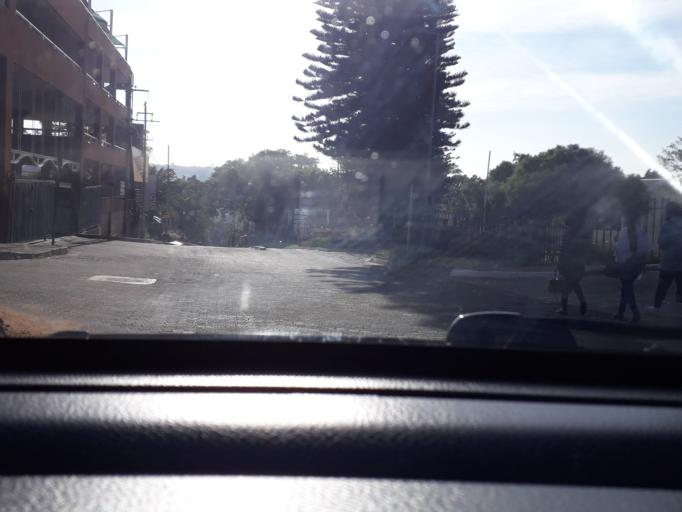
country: ZA
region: Gauteng
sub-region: City of Johannesburg Metropolitan Municipality
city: Midrand
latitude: -26.0575
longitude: 28.0609
